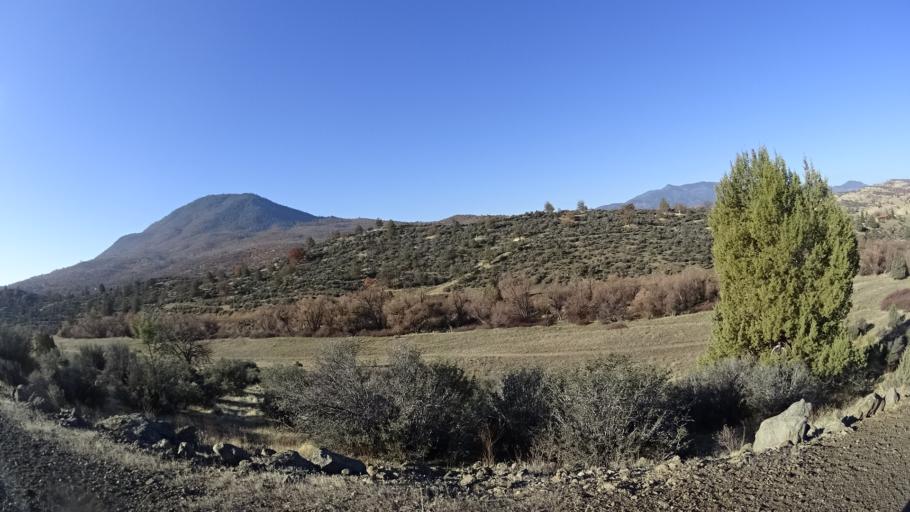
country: US
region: California
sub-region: Siskiyou County
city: Montague
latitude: 41.8957
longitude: -122.4882
